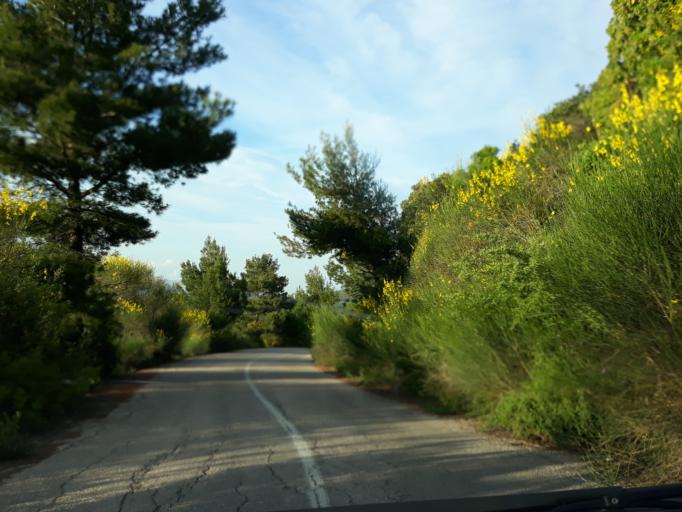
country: GR
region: Attica
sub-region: Nomarchia Anatolikis Attikis
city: Afidnes
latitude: 38.2258
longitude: 23.7916
